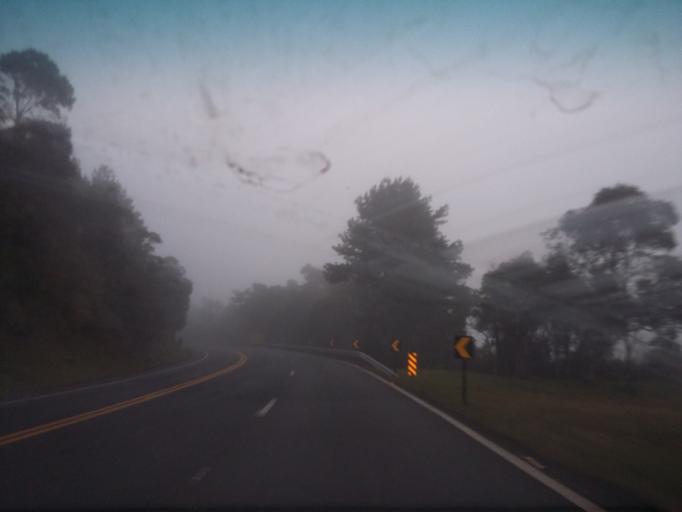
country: BR
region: Santa Catarina
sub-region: Correia Pinto
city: Correia Pinto
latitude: -27.4409
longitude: -50.3959
